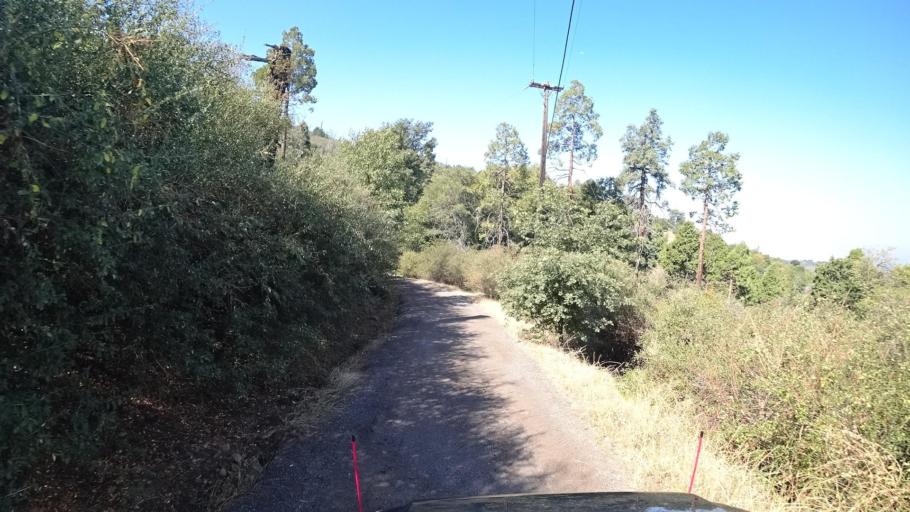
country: US
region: California
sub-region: San Diego County
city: Julian
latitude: 33.0228
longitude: -116.5861
